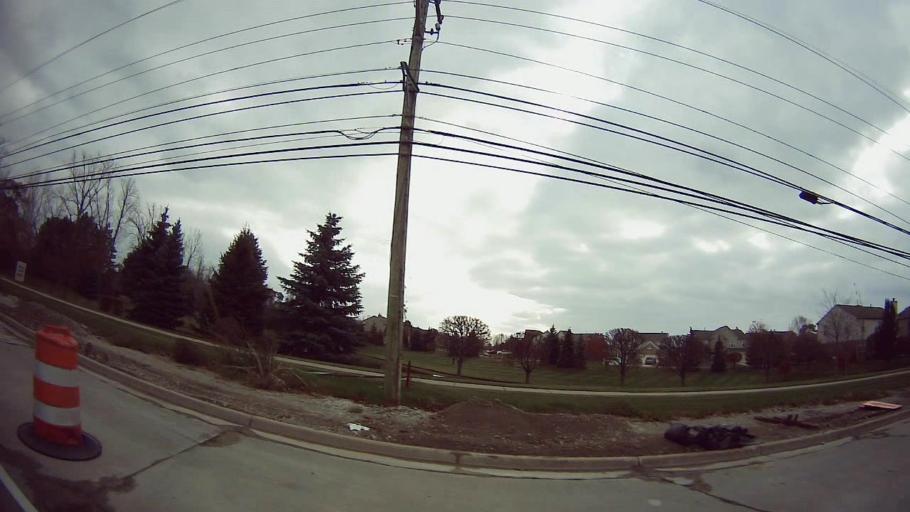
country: US
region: Michigan
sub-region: Macomb County
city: Fraser
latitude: 42.5527
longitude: -82.9720
